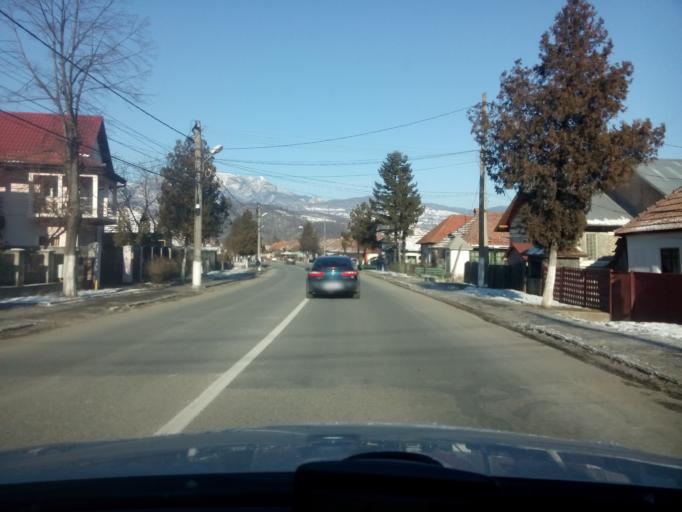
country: RO
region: Valcea
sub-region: Oras Calimanesti
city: Calimanesti
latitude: 45.2339
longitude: 24.3405
